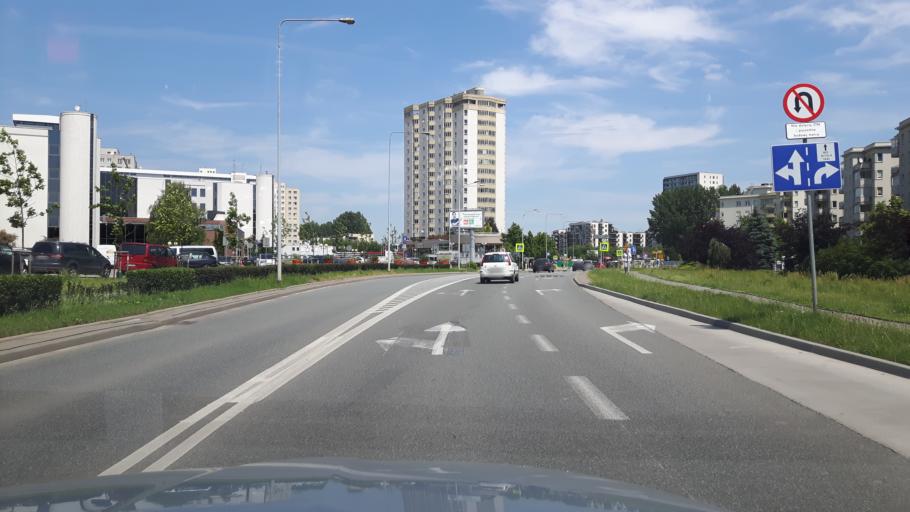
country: PL
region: Masovian Voivodeship
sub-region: Warszawa
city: Targowek
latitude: 52.2898
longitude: 21.0490
